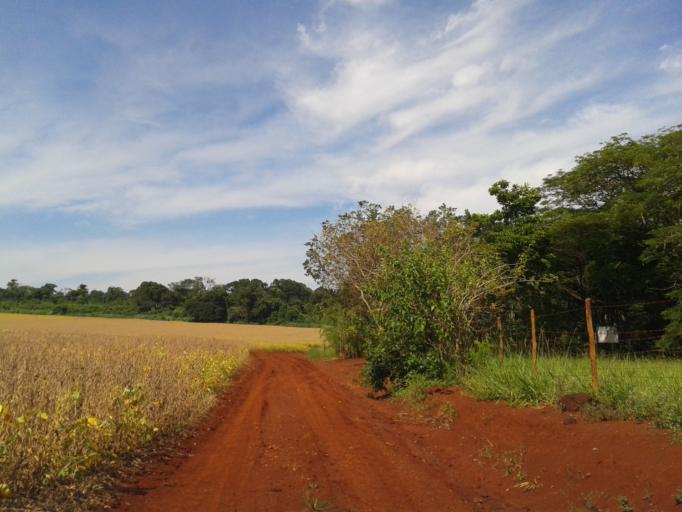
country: BR
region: Minas Gerais
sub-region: Capinopolis
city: Capinopolis
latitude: -18.6586
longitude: -49.7057
